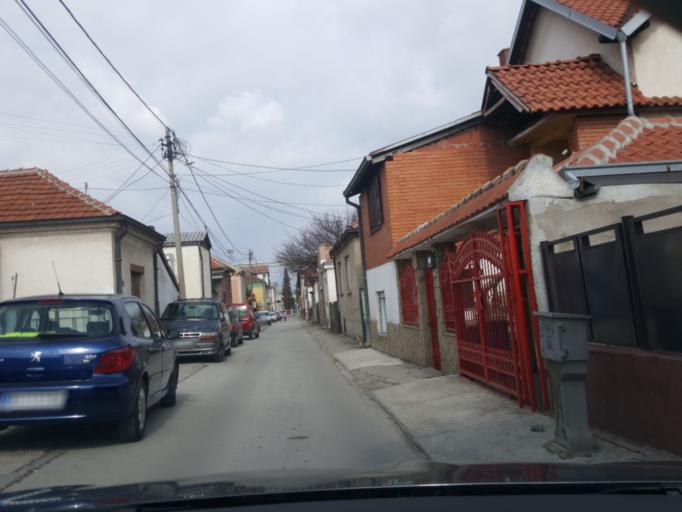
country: RS
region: Central Serbia
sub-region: Nisavski Okrug
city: Nis
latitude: 43.3137
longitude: 21.8716
